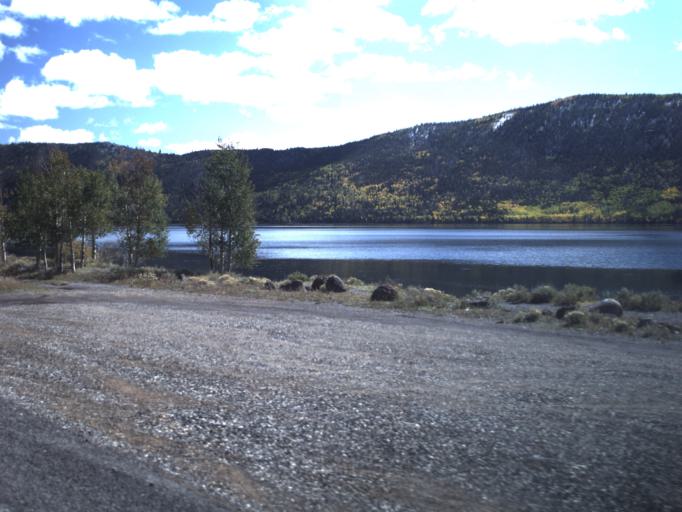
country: US
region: Utah
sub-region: Wayne County
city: Loa
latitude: 38.5581
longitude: -111.7116
